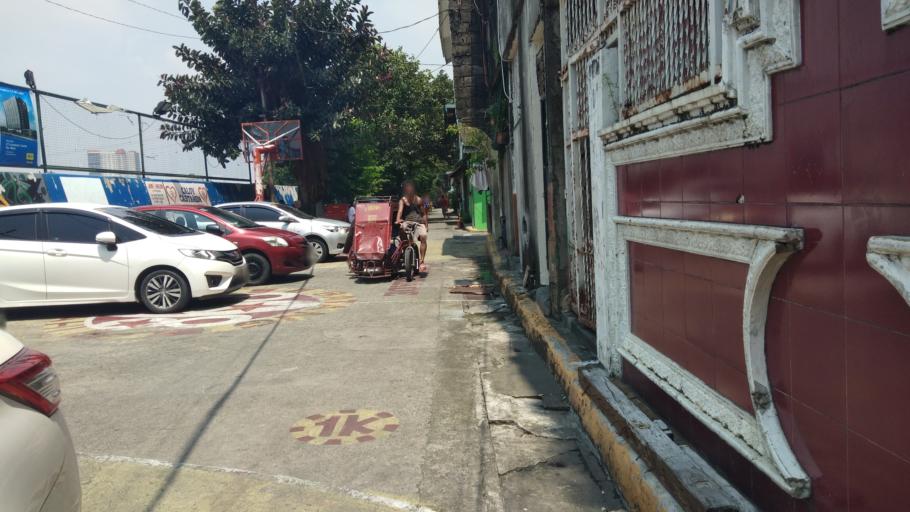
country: PH
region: Metro Manila
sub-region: San Juan
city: San Juan
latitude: 14.5880
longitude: 121.0123
